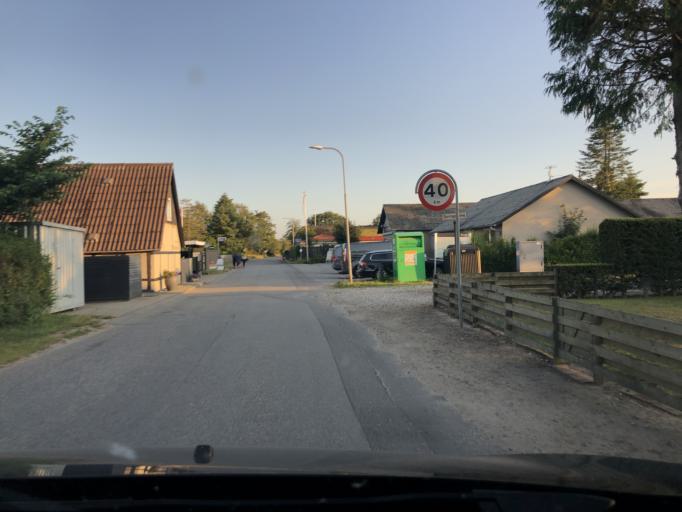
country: DK
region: South Denmark
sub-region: Fredericia Kommune
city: Fredericia
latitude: 55.6313
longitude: 9.7405
